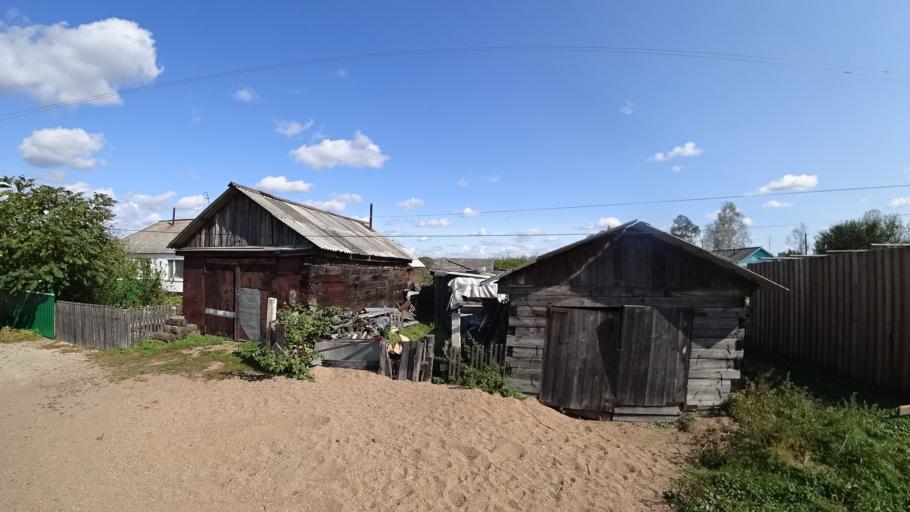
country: RU
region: Amur
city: Arkhara
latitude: 49.4029
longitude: 130.1441
